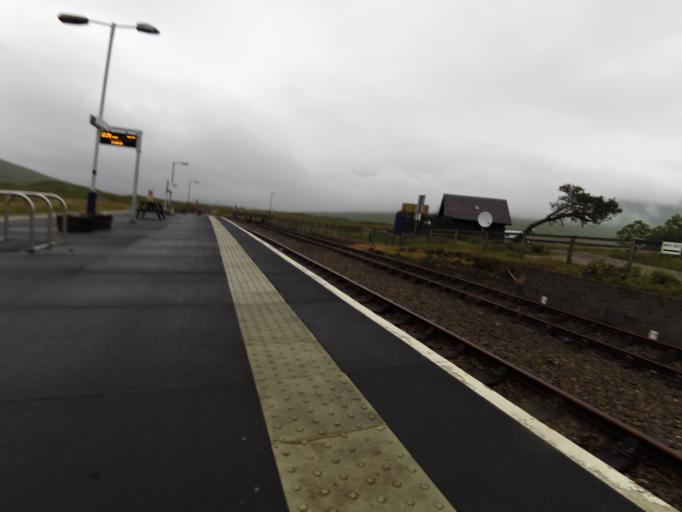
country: GB
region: Scotland
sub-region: Highland
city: Spean Bridge
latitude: 56.7603
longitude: -4.6906
